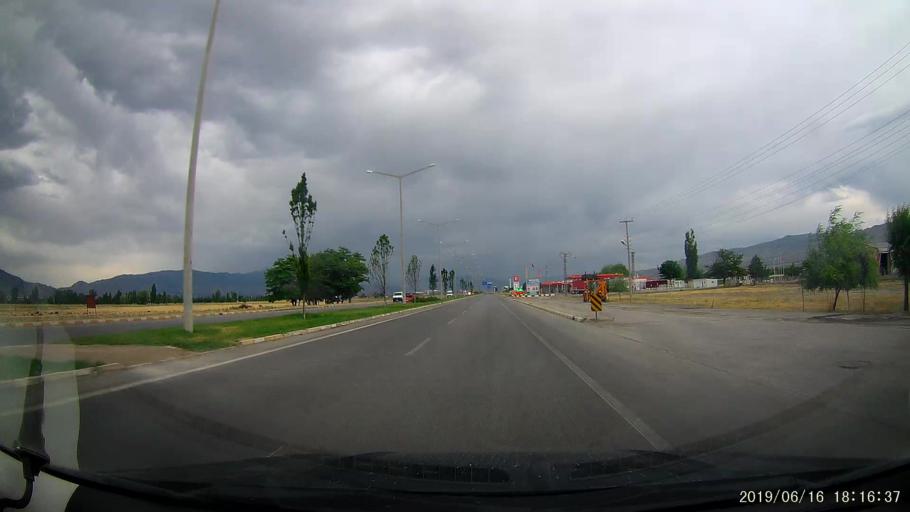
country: TR
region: Erzincan
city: Erzincan
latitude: 39.7294
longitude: 39.5454
